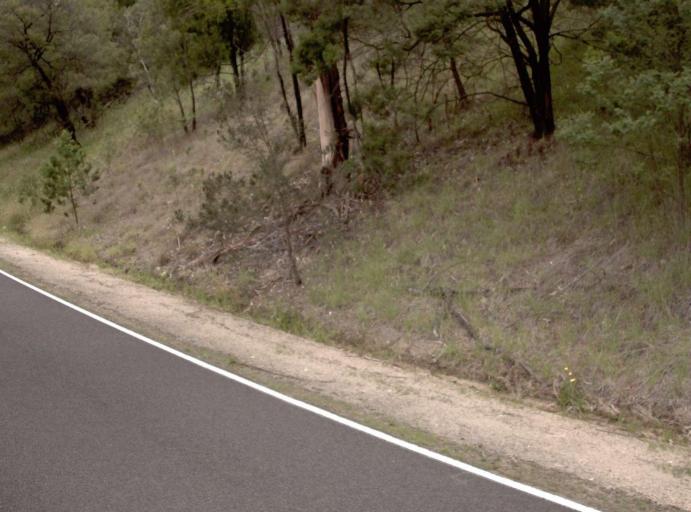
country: AU
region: New South Wales
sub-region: Bombala
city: Bombala
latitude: -37.4392
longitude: 149.1986
